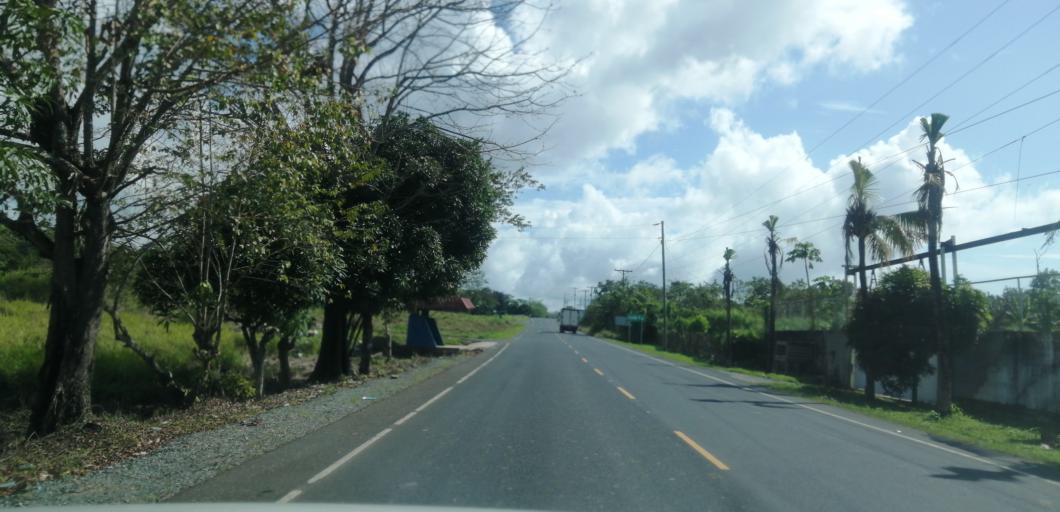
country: PA
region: Panama
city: Canita
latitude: 9.2208
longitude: -78.9000
